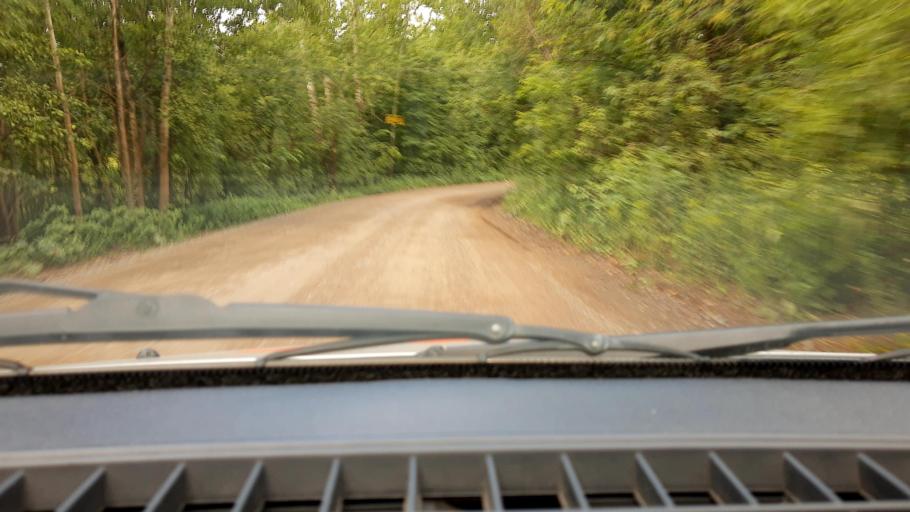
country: RU
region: Bashkortostan
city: Ufa
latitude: 54.6779
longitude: 56.0617
